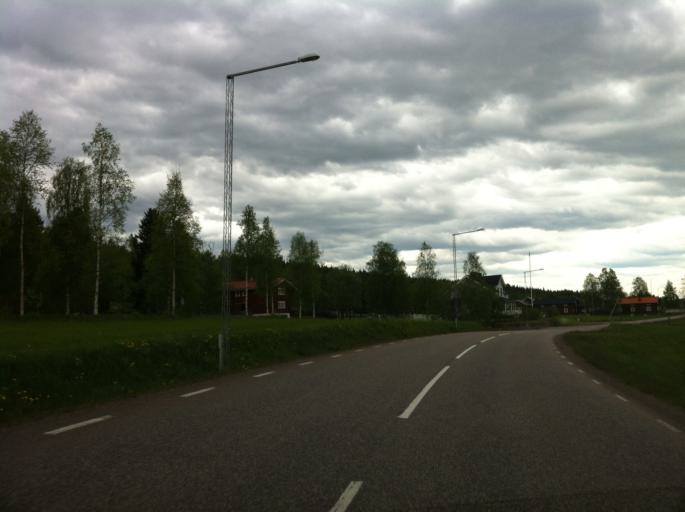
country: SE
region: Dalarna
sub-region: Malung-Saelens kommun
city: Malung
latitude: 61.1437
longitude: 13.2759
